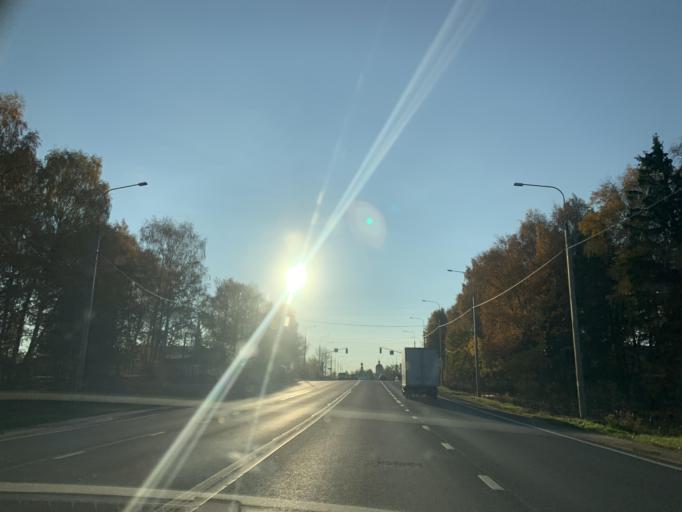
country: RU
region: Jaroslavl
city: Konstantinovskiy
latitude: 57.7665
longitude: 39.6780
